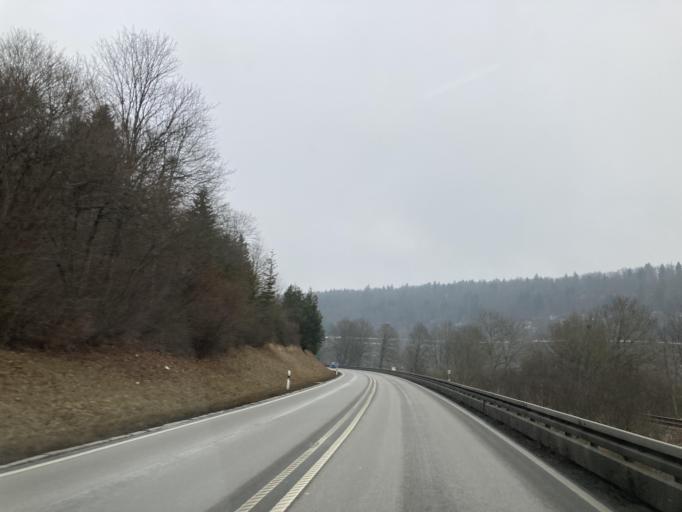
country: DE
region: Baden-Wuerttemberg
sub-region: Freiburg Region
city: Immendingen
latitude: 47.9326
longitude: 8.7547
